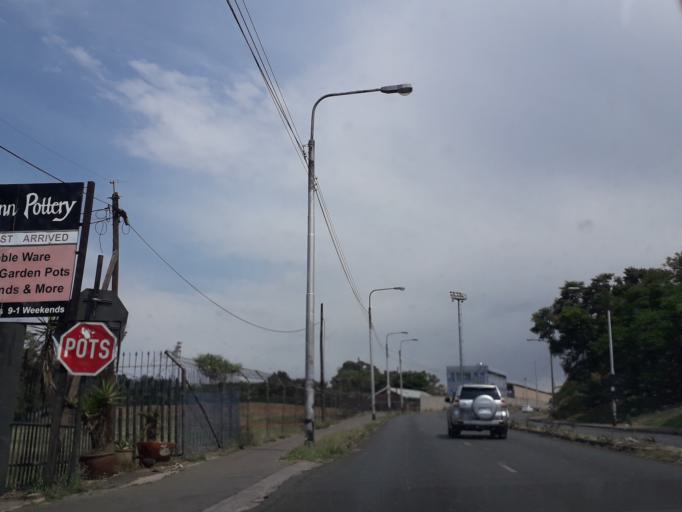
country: ZA
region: Gauteng
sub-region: City of Johannesburg Metropolitan Municipality
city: Johannesburg
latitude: -26.1910
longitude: 28.0199
